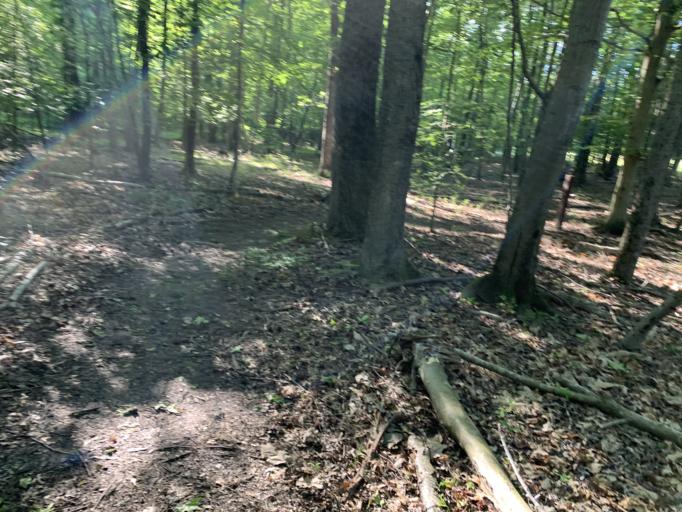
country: US
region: Maryland
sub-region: Cecil County
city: Elkton
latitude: 39.5729
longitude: -75.8844
